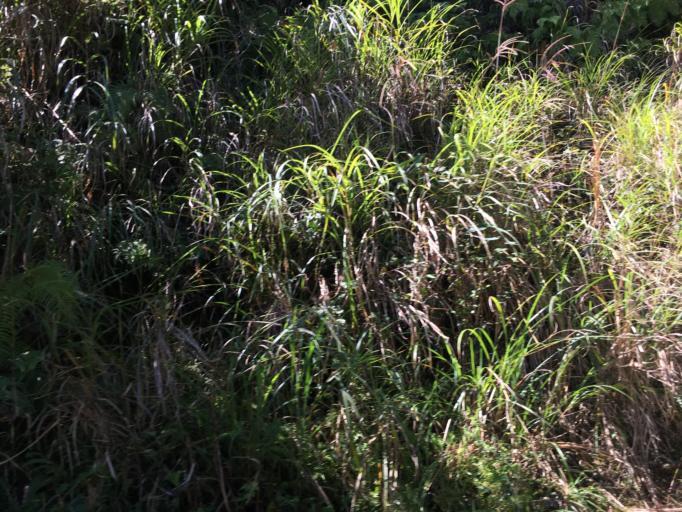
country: TW
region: Taiwan
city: Daxi
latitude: 24.5510
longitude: 121.3977
